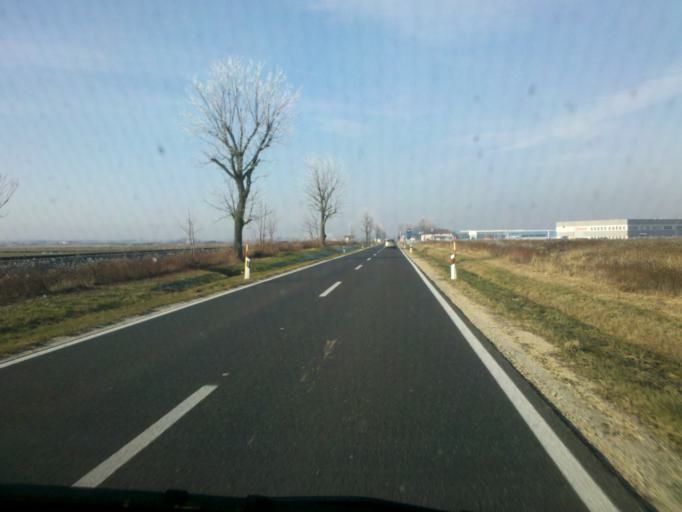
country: HR
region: Koprivnicko-Krizevacka
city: Kalinovac
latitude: 46.0097
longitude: 17.1012
